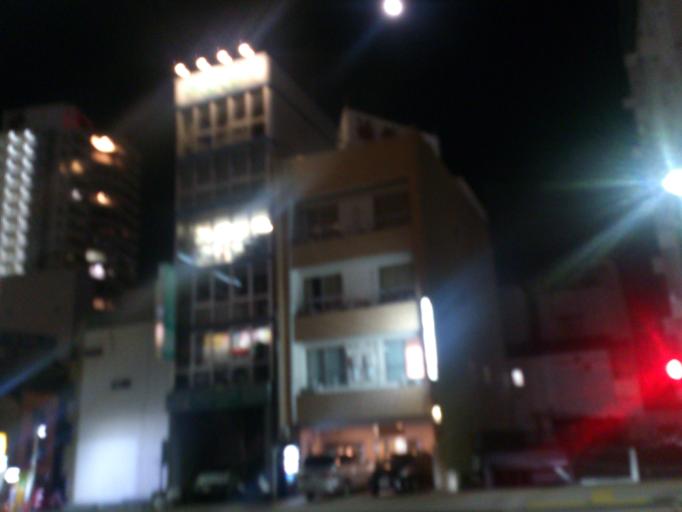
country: JP
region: Hiroshima
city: Hiroshima-shi
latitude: 34.3962
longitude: 132.4713
